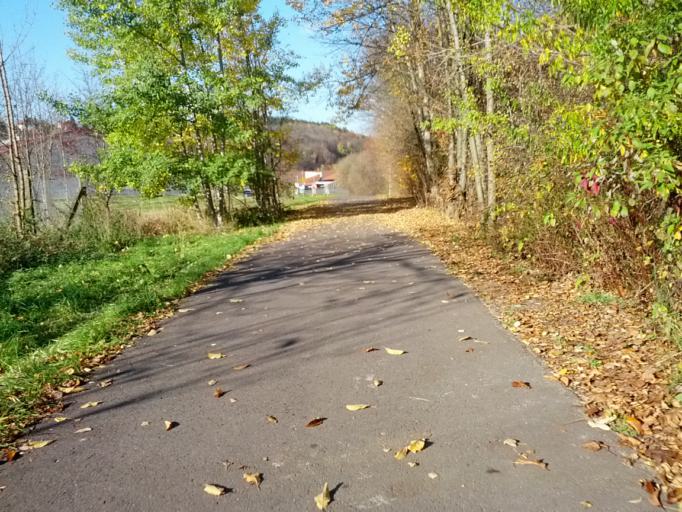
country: DE
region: Thuringia
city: Thal
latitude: 50.9185
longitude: 10.3984
